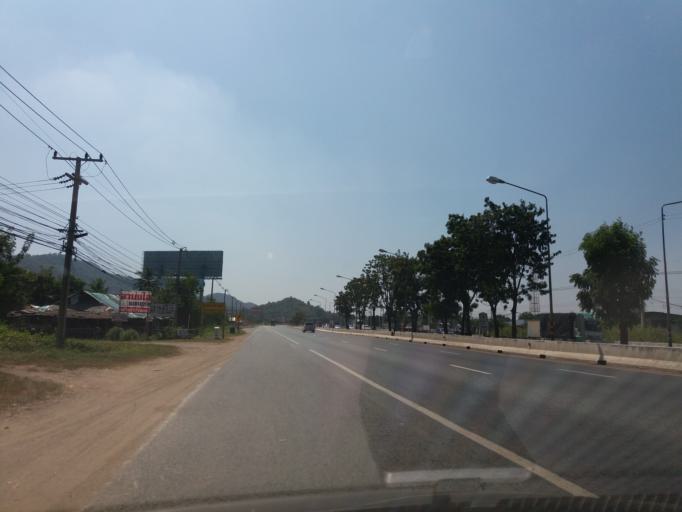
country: TH
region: Nakhon Sawan
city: Krok Phra
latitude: 15.5497
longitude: 100.1281
